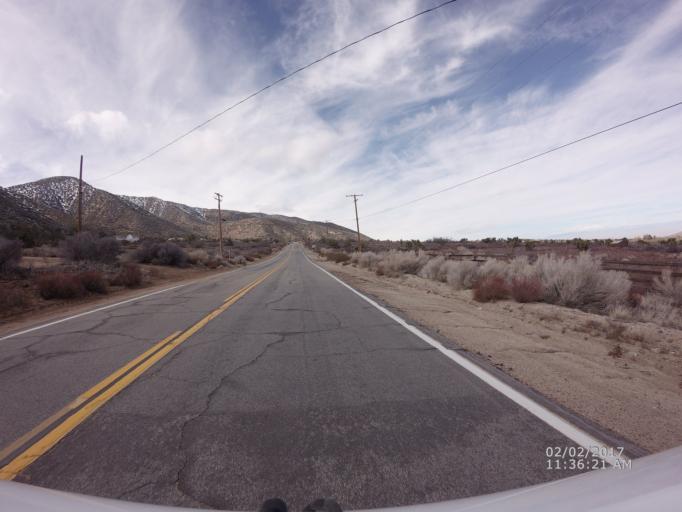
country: US
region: California
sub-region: Los Angeles County
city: Littlerock
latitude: 34.4265
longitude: -117.9065
